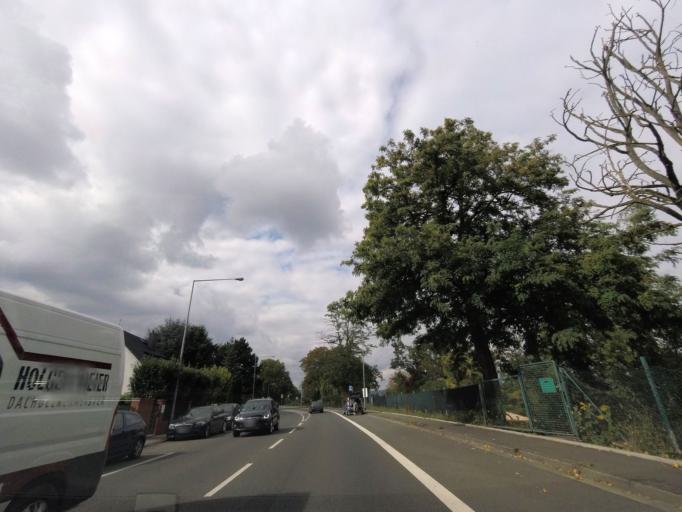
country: DE
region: Hesse
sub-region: Regierungsbezirk Darmstadt
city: Wiesbaden
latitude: 50.0617
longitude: 8.2474
